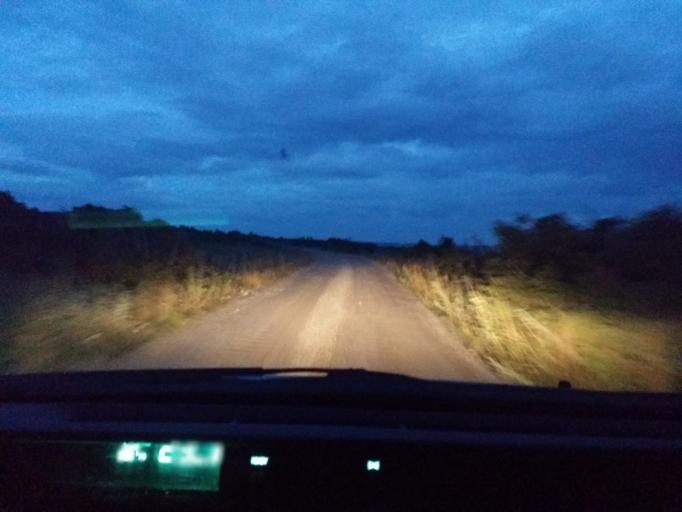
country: SE
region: Kalmar
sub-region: Borgholms Kommun
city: Borgholm
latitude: 57.1408
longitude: 16.9066
